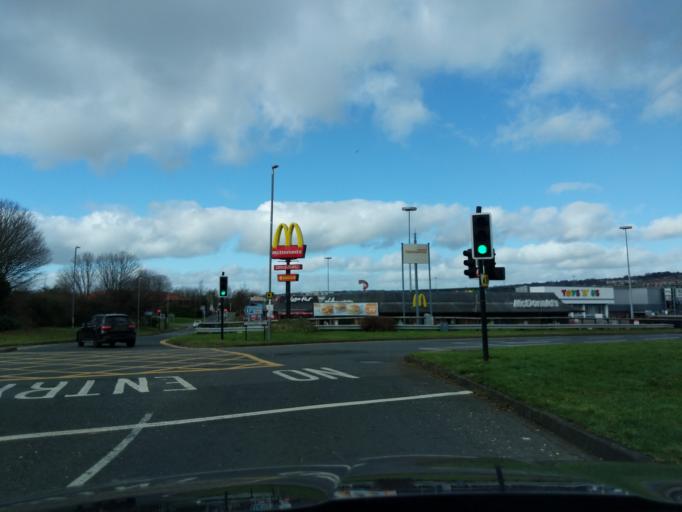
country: GB
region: England
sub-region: Gateshead
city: Whickham
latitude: 54.9576
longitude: -1.6746
